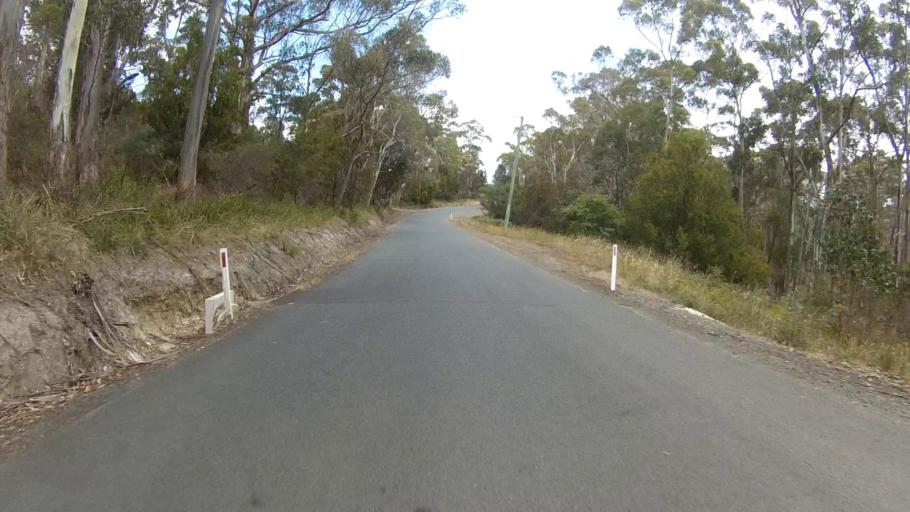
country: AU
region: Tasmania
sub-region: Kingborough
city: Blackmans Bay
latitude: -43.0244
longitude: 147.3135
